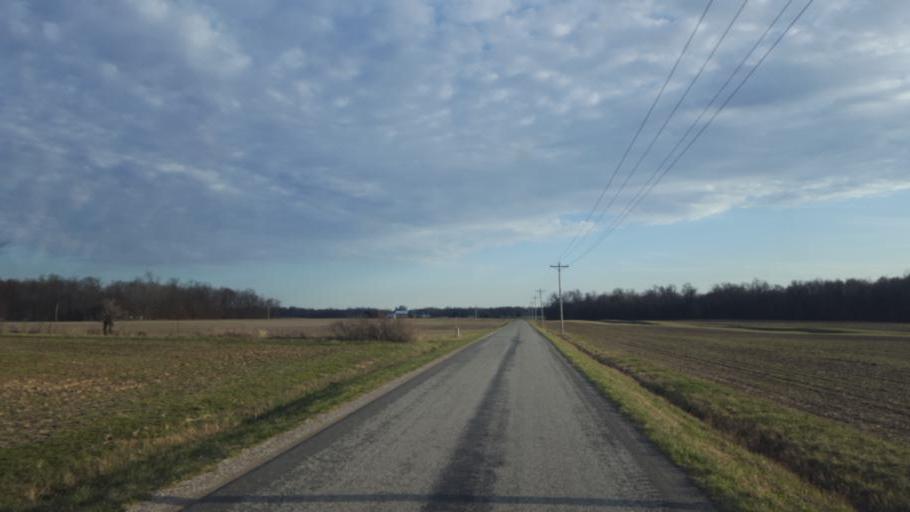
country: US
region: Ohio
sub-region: Marion County
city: Marion
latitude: 40.6119
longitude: -82.9910
